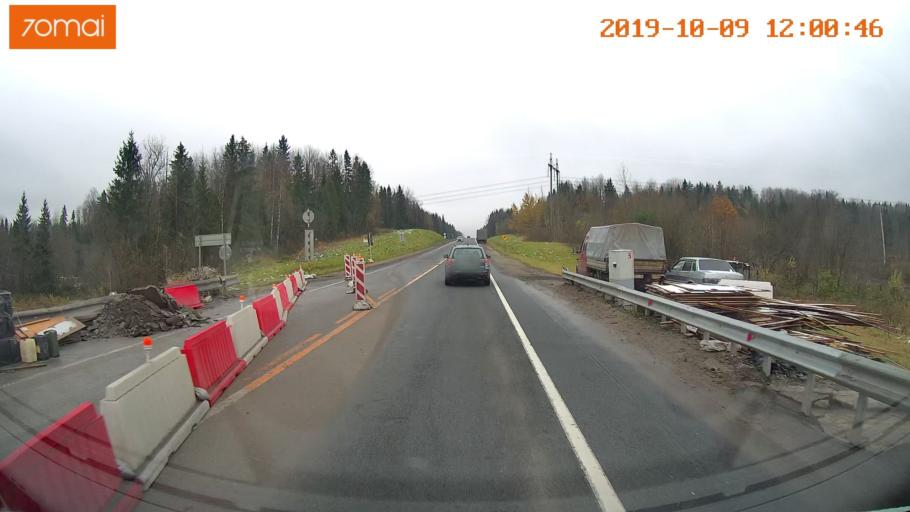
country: RU
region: Vologda
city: Gryazovets
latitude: 58.6945
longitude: 40.3006
